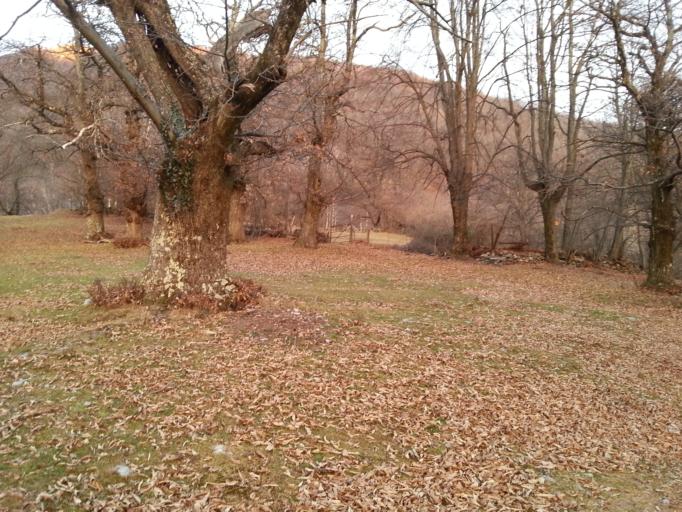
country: CH
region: Ticino
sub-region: Lugano District
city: Gravesano
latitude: 46.0493
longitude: 8.8864
